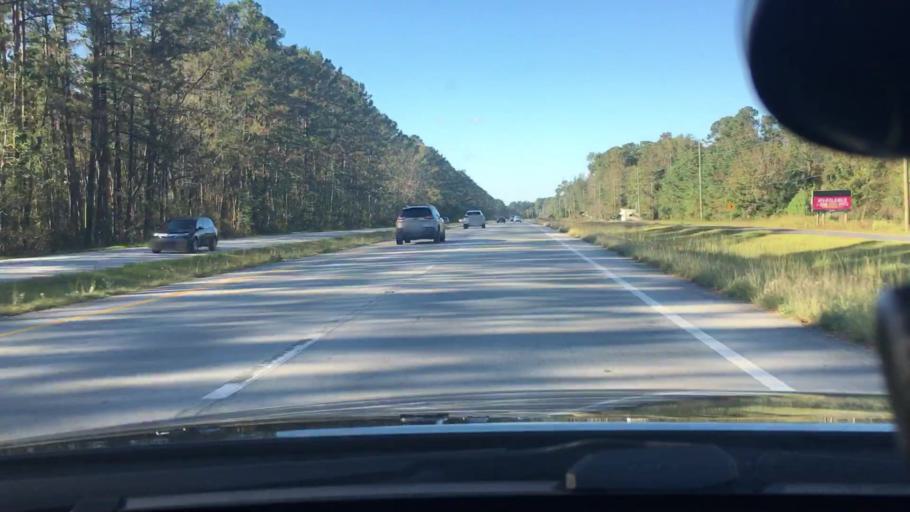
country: US
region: North Carolina
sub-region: Craven County
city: Neuse Forest
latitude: 34.9786
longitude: -76.9763
